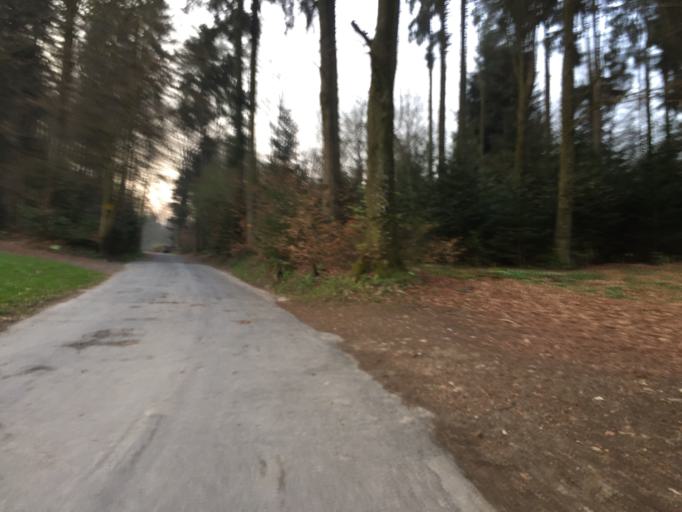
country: CH
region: Bern
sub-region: Bern-Mittelland District
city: Koniz
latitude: 46.9193
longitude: 7.4262
